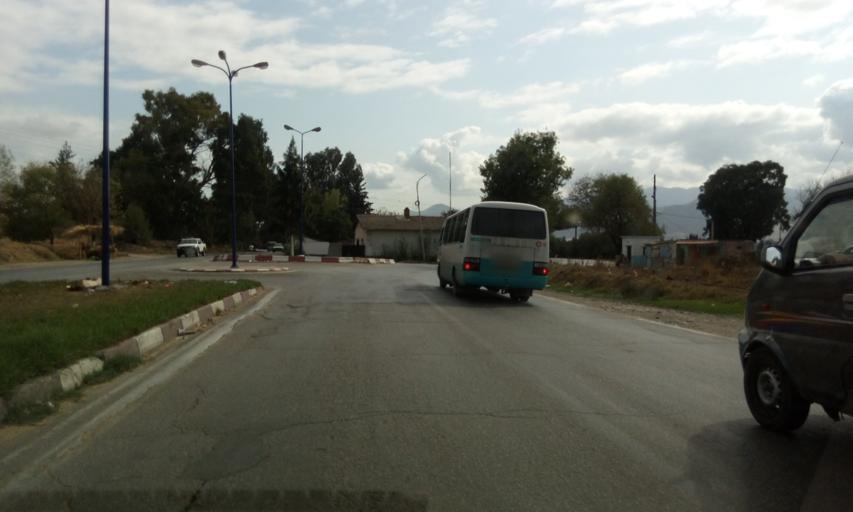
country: DZ
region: Bejaia
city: El Kseur
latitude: 36.6740
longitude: 4.8774
